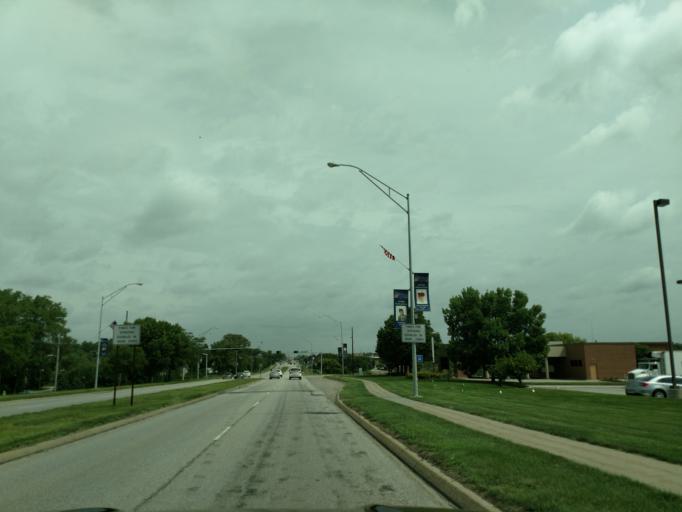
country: US
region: Nebraska
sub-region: Sarpy County
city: La Vista
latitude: 41.1822
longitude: -96.0430
